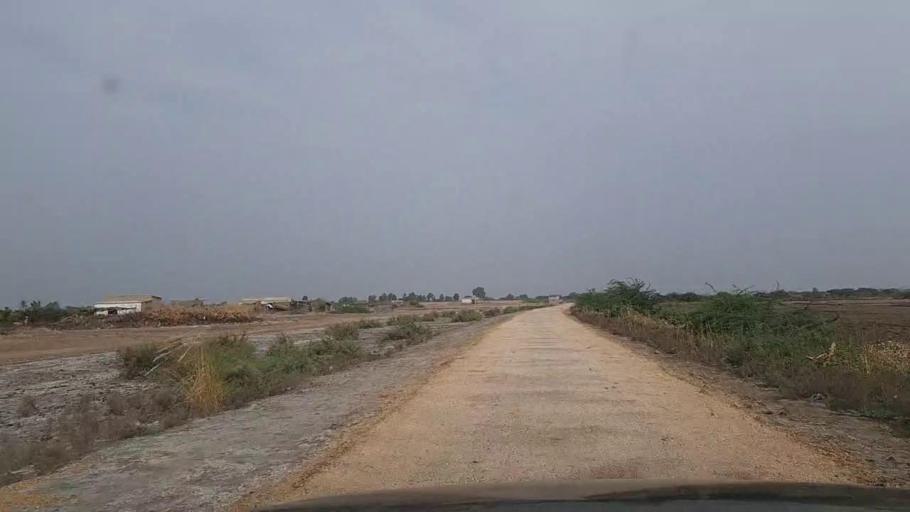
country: PK
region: Sindh
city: Thatta
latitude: 24.7490
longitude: 67.8266
